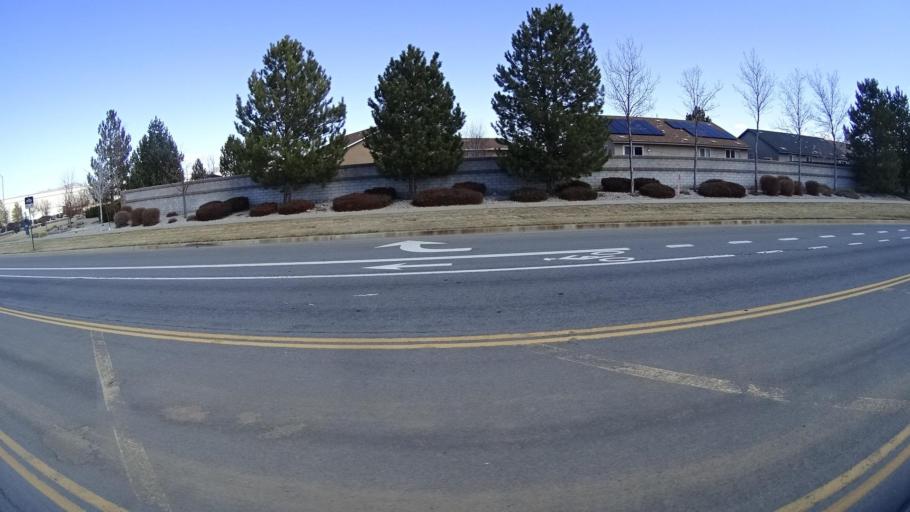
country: US
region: Nevada
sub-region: Washoe County
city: Lemmon Valley
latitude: 39.6417
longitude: -119.8622
